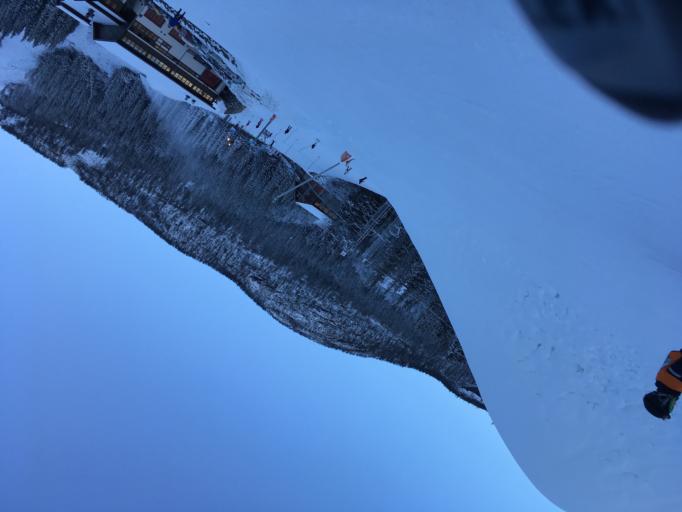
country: NO
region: Buskerud
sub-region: Hemsedal
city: Hemsedal
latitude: 60.8616
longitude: 8.5137
